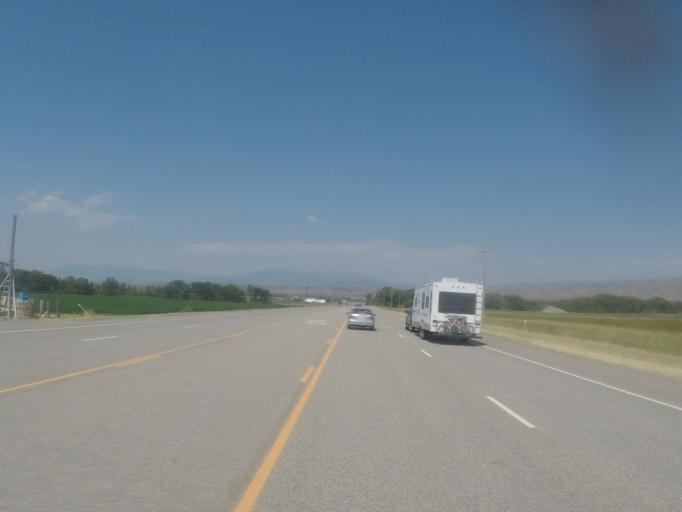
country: US
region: Montana
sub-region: Broadwater County
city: Townsend
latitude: 46.1490
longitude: -111.4692
